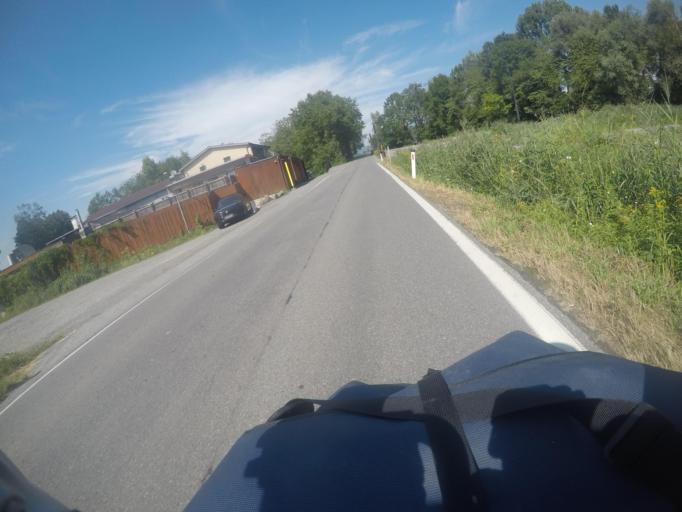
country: AT
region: Vorarlberg
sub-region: Politischer Bezirk Bregenz
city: Hard
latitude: 47.4453
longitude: 9.6958
